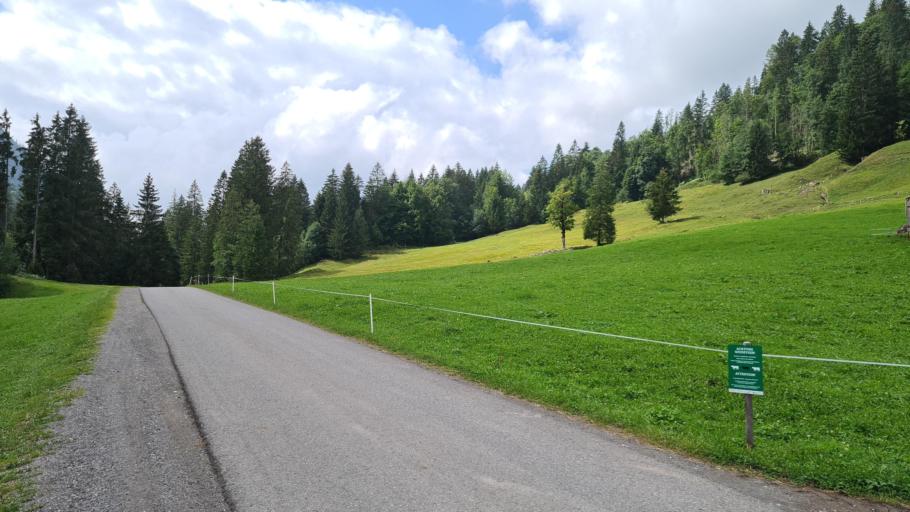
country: AT
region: Vorarlberg
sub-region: Politischer Bezirk Bregenz
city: Au
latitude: 47.3736
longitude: 10.0064
